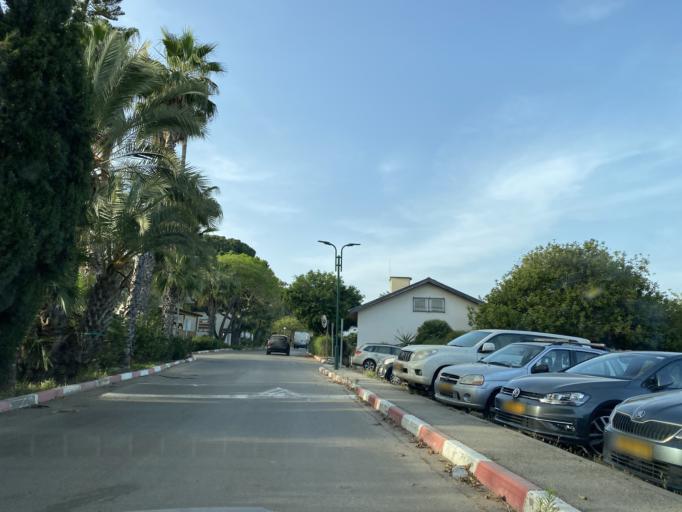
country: IL
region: Tel Aviv
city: Herzliyya
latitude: 32.1562
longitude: 34.8316
